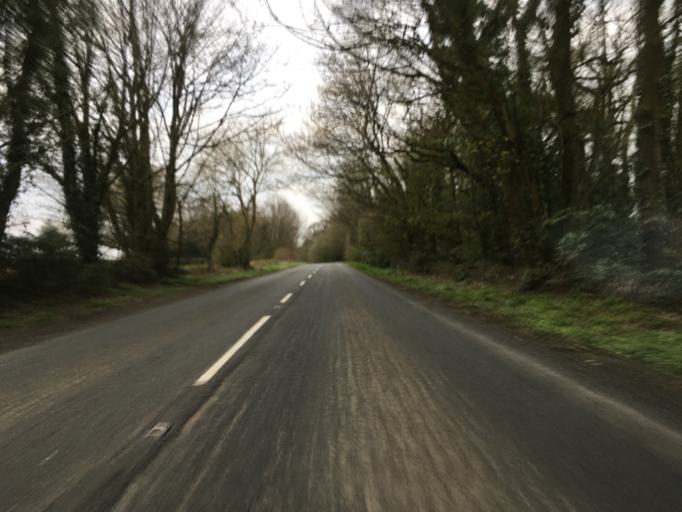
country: GB
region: England
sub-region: Gloucestershire
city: Nailsworth
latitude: 51.6293
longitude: -2.2569
